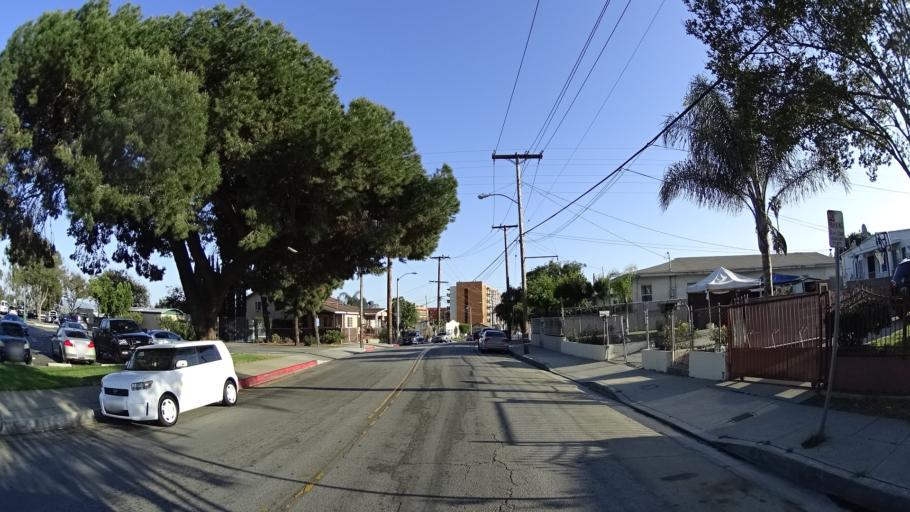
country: US
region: California
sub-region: Los Angeles County
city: Belvedere
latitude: 34.0482
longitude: -118.1801
